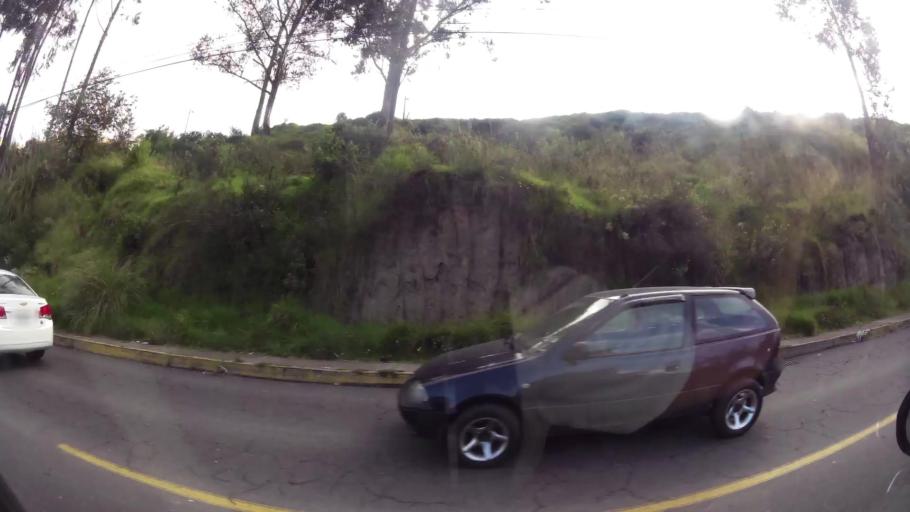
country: EC
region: Pichincha
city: Quito
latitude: -0.2466
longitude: -78.4964
